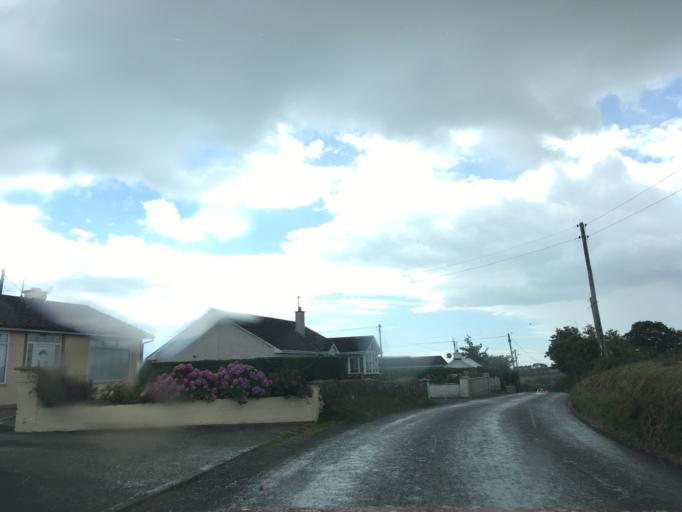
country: IE
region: Munster
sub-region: County Cork
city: Crosshaven
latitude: 51.7877
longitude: -8.3057
